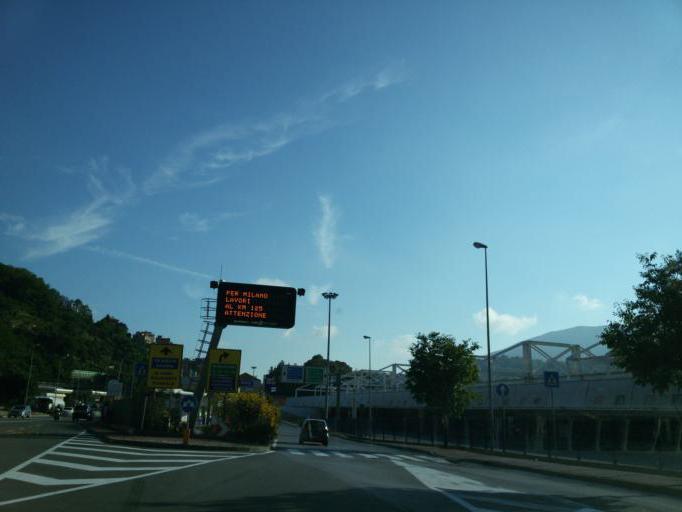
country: IT
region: Liguria
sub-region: Provincia di Genova
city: Manesseno
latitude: 44.4669
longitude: 8.9060
